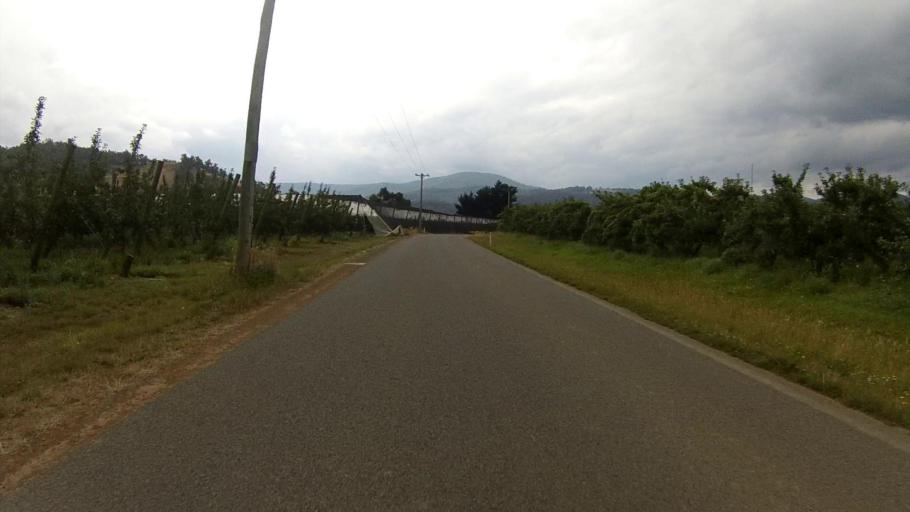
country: AU
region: Tasmania
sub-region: Huon Valley
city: Huonville
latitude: -42.9912
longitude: 147.0623
